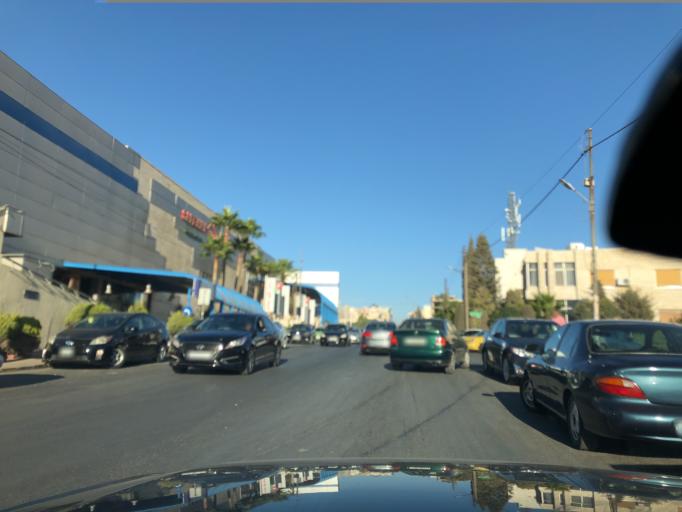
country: JO
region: Amman
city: Wadi as Sir
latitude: 31.9543
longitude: 35.8556
